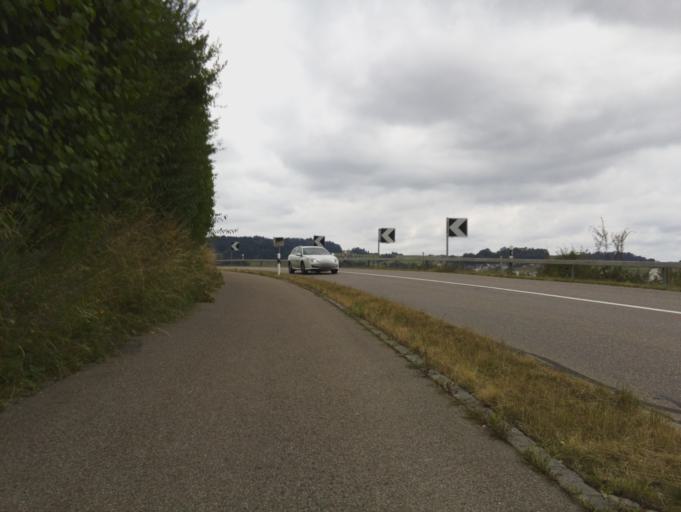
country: CH
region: Saint Gallen
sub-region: Wahlkreis Toggenburg
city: Lutisburg
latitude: 47.4086
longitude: 9.0822
